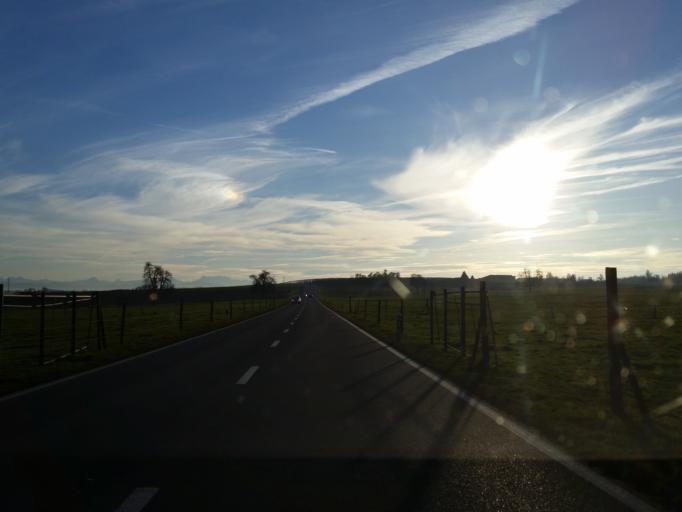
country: CH
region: Thurgau
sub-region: Weinfelden District
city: Erlen
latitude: 47.5344
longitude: 9.2646
